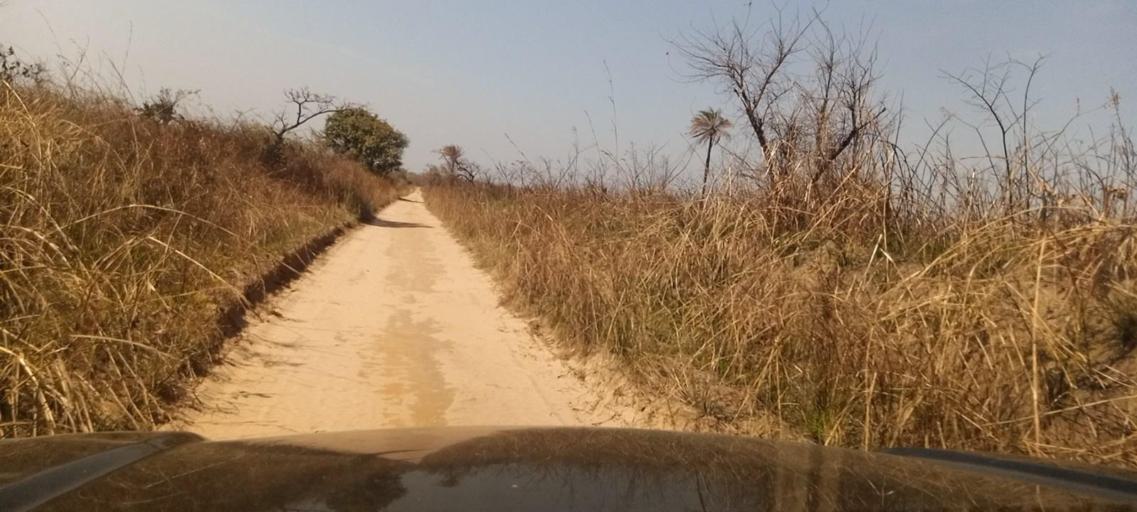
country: CD
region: Kasai-Oriental
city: Kabinda
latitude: -5.7953
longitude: 25.0310
